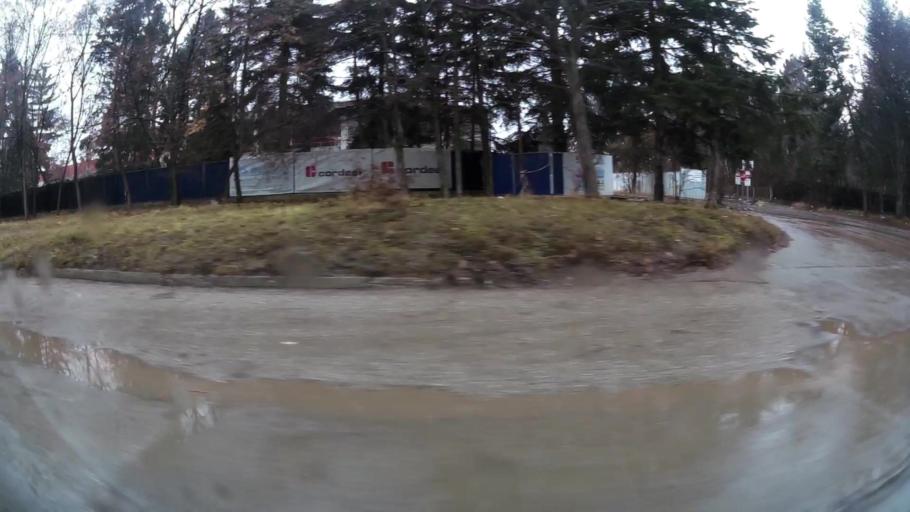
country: BG
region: Sofia-Capital
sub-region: Stolichna Obshtina
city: Sofia
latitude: 42.6372
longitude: 23.4070
